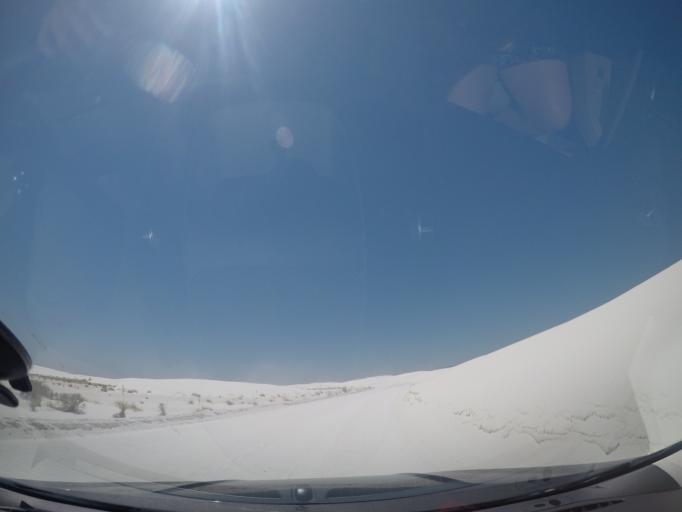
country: US
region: New Mexico
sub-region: Otero County
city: Holloman Air Force Base
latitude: 32.8096
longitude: -106.2618
